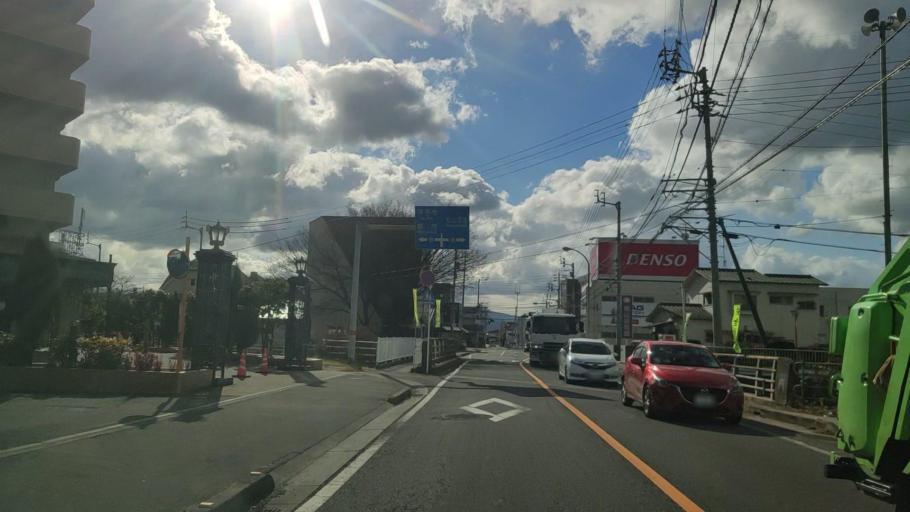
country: JP
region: Ehime
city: Masaki-cho
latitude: 33.8295
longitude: 132.7085
